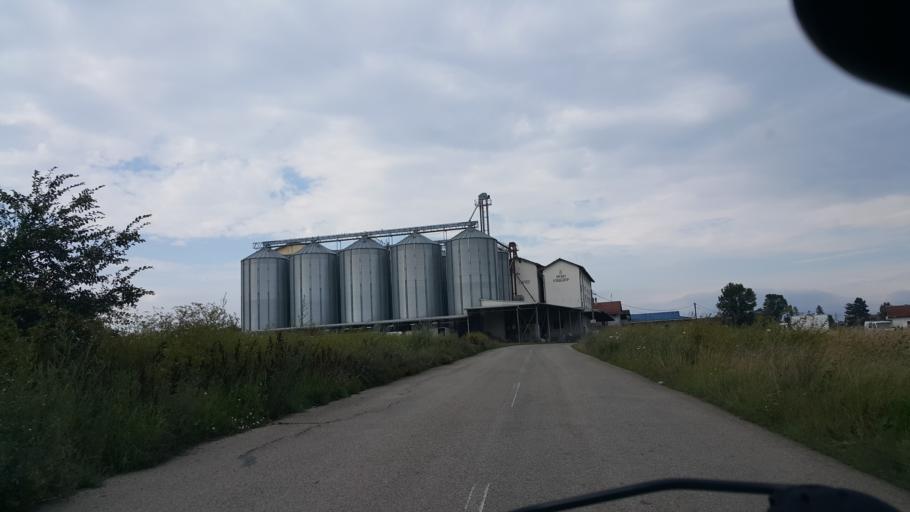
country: RS
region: Central Serbia
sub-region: Toplicki Okrug
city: Blace
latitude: 43.2593
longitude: 21.2678
